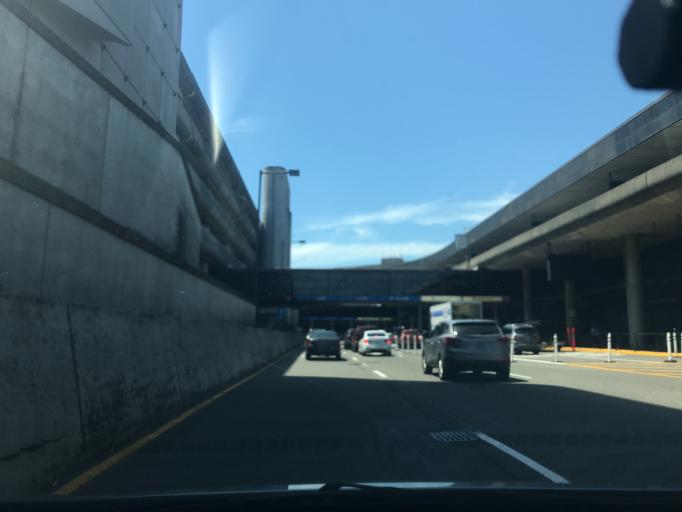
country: US
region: Washington
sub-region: King County
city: SeaTac
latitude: 47.4446
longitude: -122.3003
